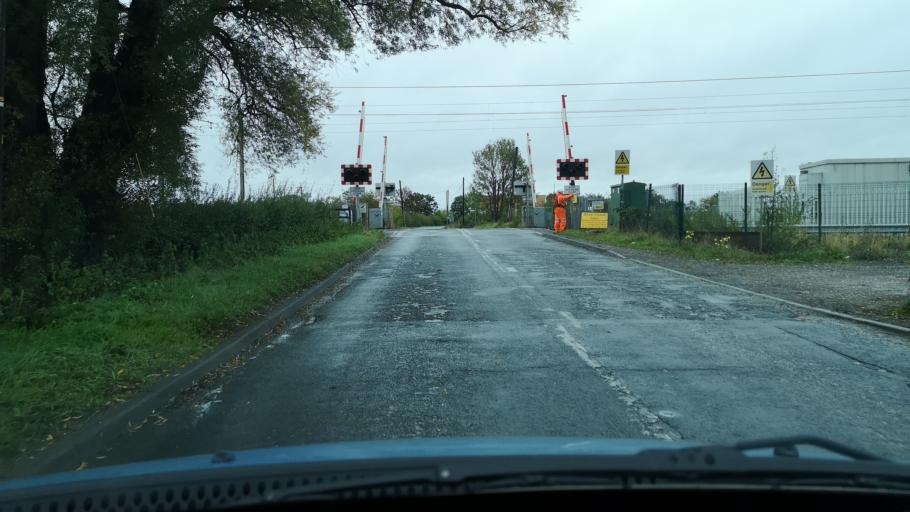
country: GB
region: England
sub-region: Doncaster
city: Moss
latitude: 53.6225
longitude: -1.1136
